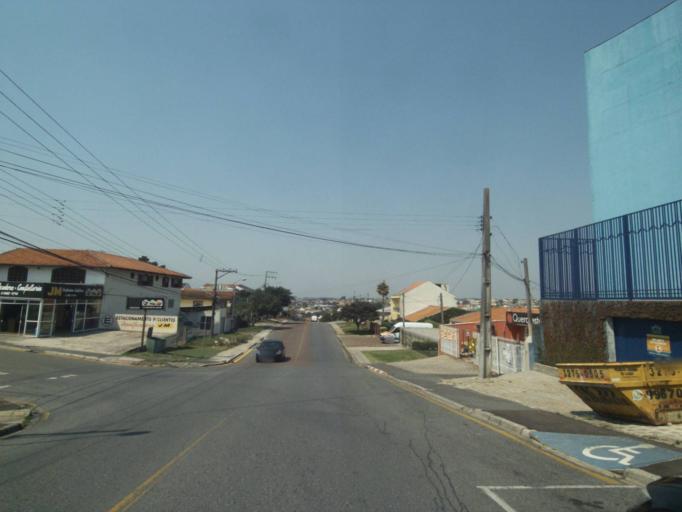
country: BR
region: Parana
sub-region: Sao Jose Dos Pinhais
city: Sao Jose dos Pinhais
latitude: -25.5072
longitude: -49.2738
